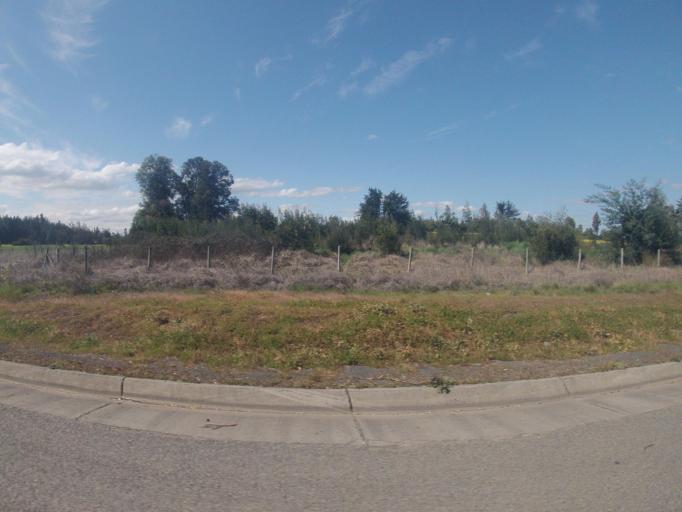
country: CL
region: Biobio
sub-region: Provincia de Biobio
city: Los Angeles
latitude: -37.4463
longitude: -72.4040
